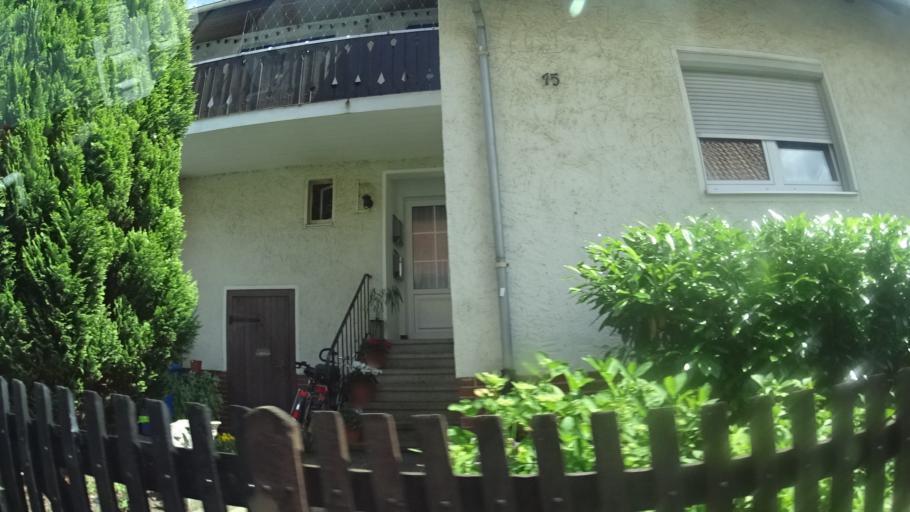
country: DE
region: Lower Saxony
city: Harsum
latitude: 52.1749
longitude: 9.9941
